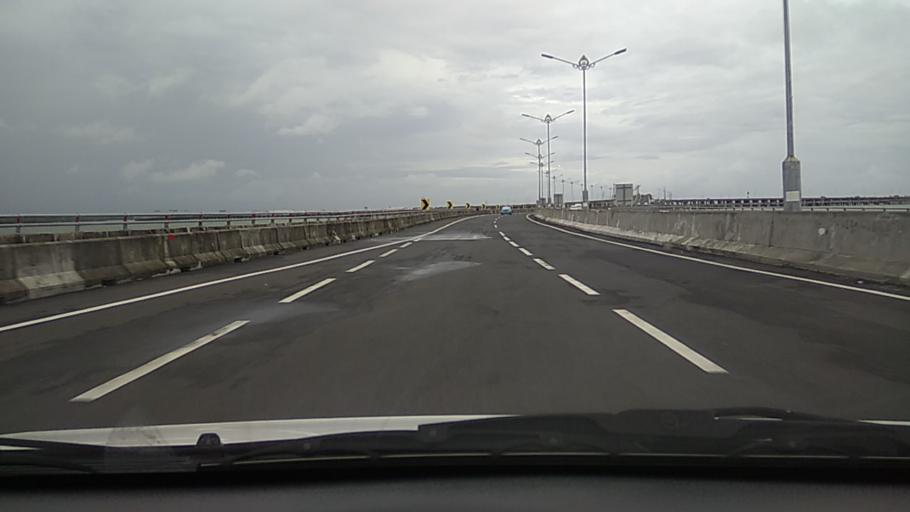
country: ID
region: Bali
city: Kelanabian
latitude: -8.7442
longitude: 115.1888
